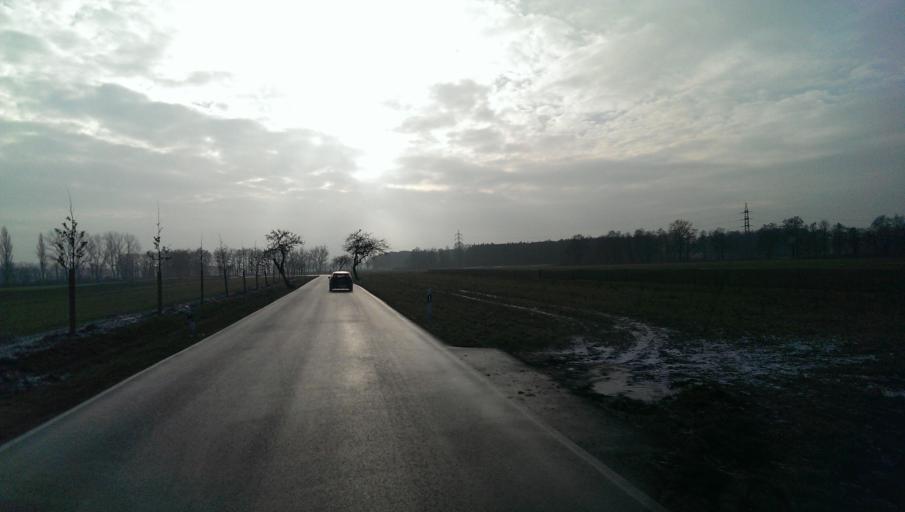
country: DE
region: Saxony
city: Nauwalde
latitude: 51.4331
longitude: 13.4624
